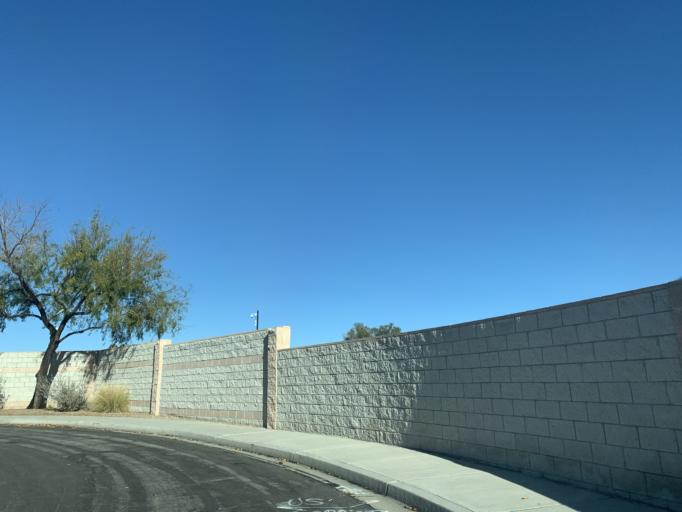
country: US
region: Nevada
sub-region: Clark County
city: Spring Valley
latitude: 36.1240
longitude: -115.2852
